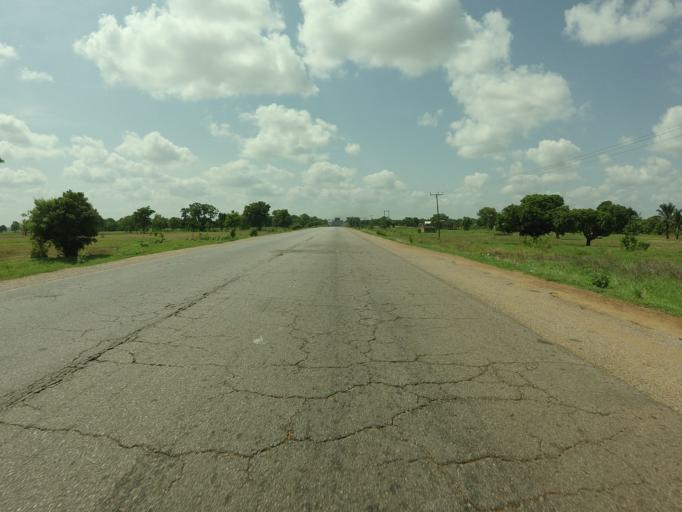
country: GH
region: Northern
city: Savelugu
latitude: 9.5593
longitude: -0.8365
